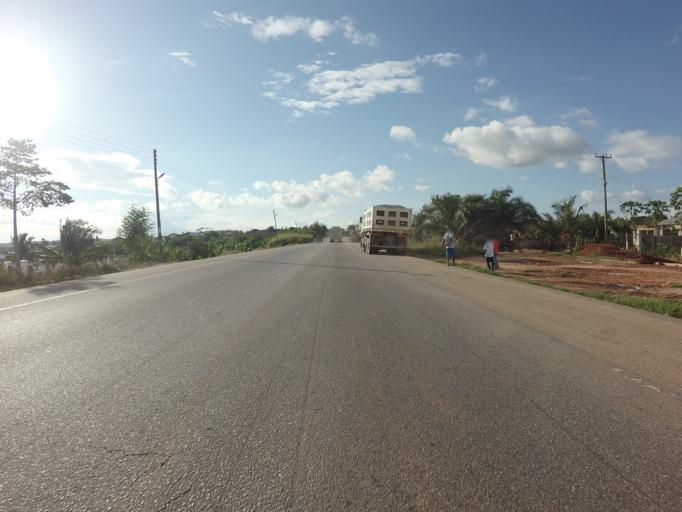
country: GH
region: Ashanti
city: Tafo
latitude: 6.9132
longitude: -1.6580
